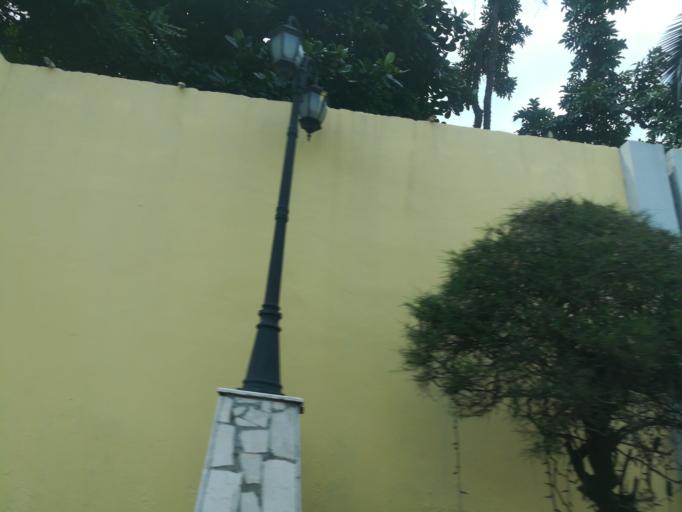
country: NG
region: Lagos
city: Ikeja
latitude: 6.6050
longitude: 3.3618
